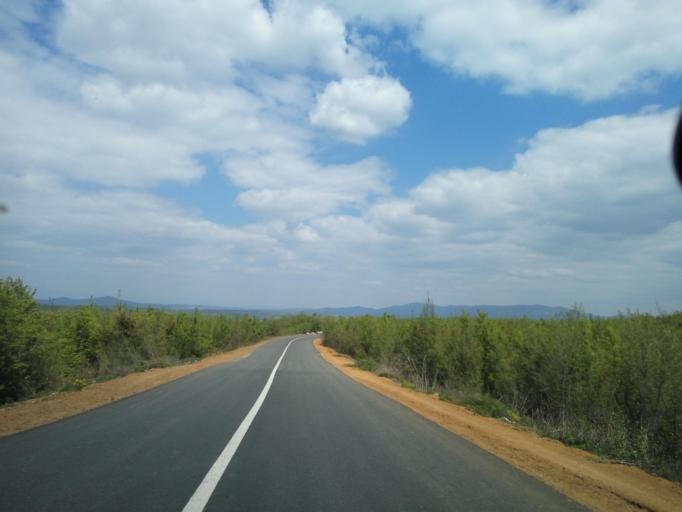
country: XK
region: Gjakova
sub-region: Komuna e Gjakoves
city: Gjakove
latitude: 42.3221
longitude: 20.4511
